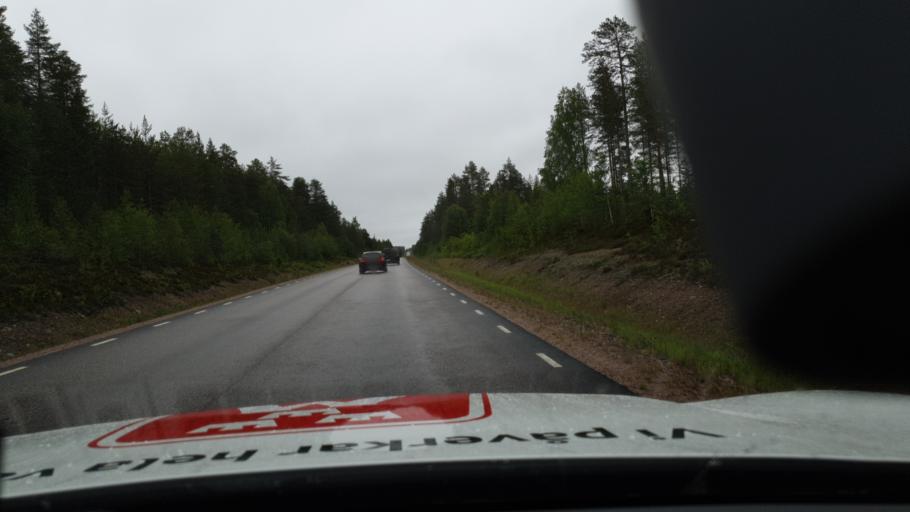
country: SE
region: Norrbotten
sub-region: Overtornea Kommun
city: OEvertornea
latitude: 66.5138
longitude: 23.7376
